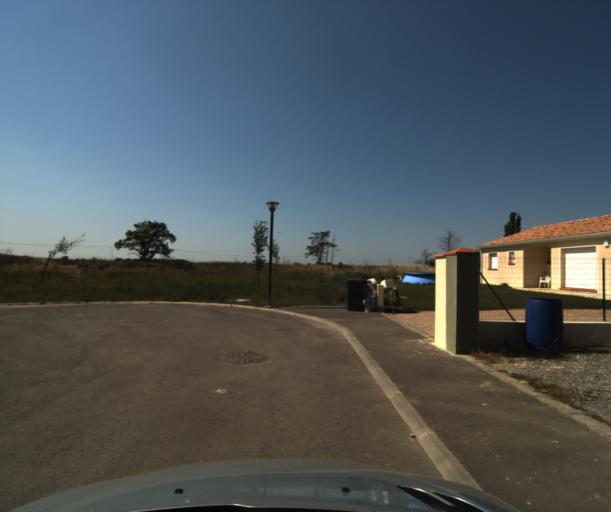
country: FR
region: Midi-Pyrenees
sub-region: Departement de la Haute-Garonne
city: Muret
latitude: 43.4682
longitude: 1.3760
